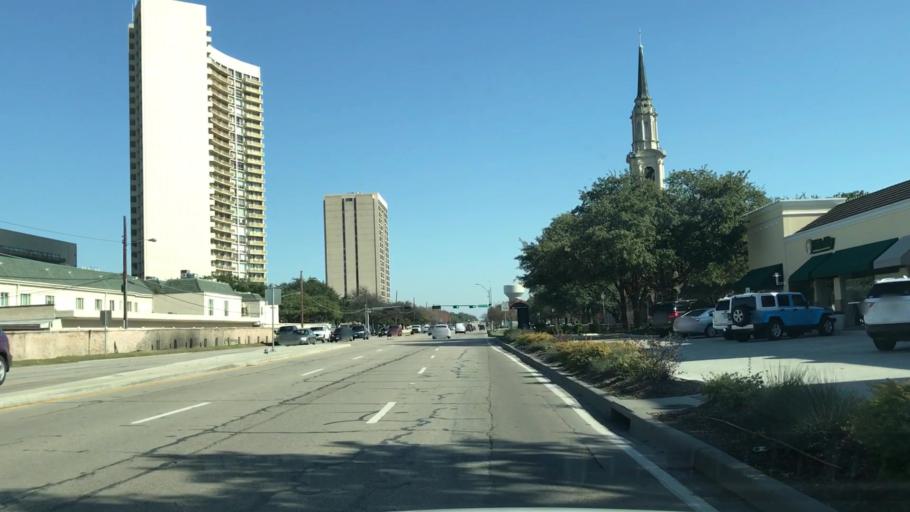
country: US
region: Texas
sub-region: Dallas County
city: University Park
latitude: 32.8655
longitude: -96.8027
